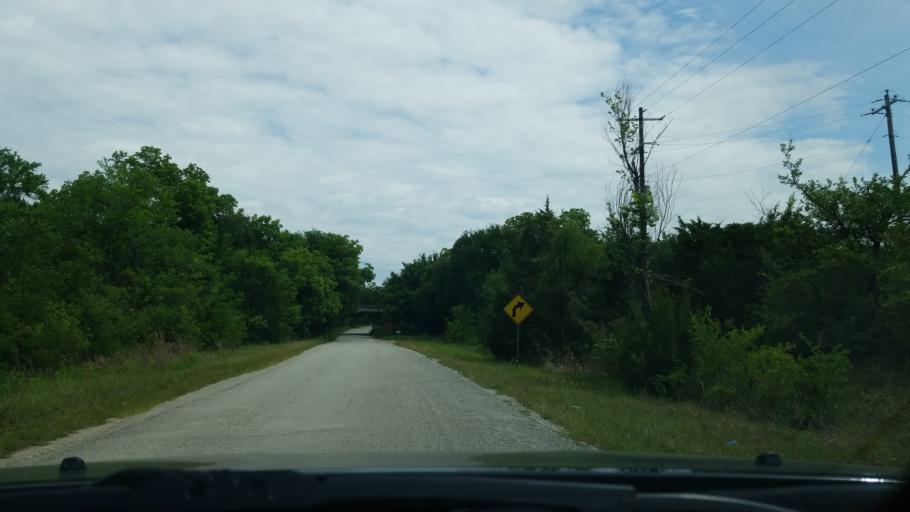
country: US
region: Texas
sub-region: Denton County
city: Sanger
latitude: 33.3186
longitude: -97.1757
